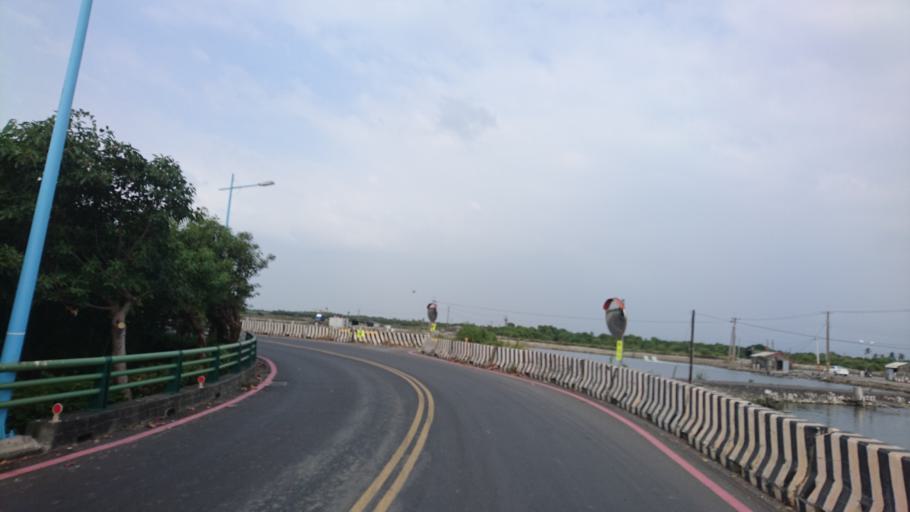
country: TW
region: Taiwan
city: Fengshan
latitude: 22.4320
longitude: 120.4916
